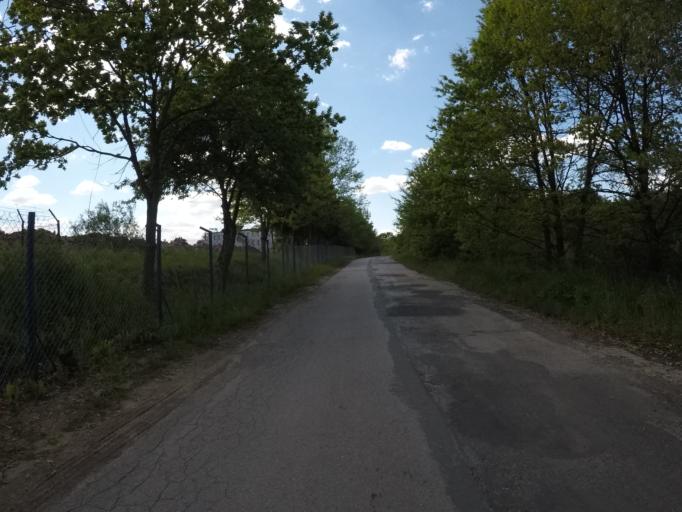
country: PL
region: Swietokrzyskie
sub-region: Powiat kielecki
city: Kostomloty Pierwsze
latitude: 50.9081
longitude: 20.5933
